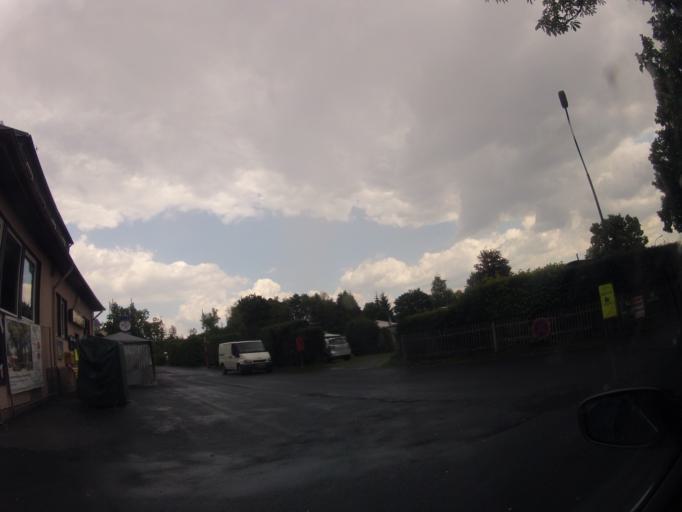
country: DE
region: Bavaria
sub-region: Upper Franconia
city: Weissenstadt
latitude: 50.1082
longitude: 11.8758
